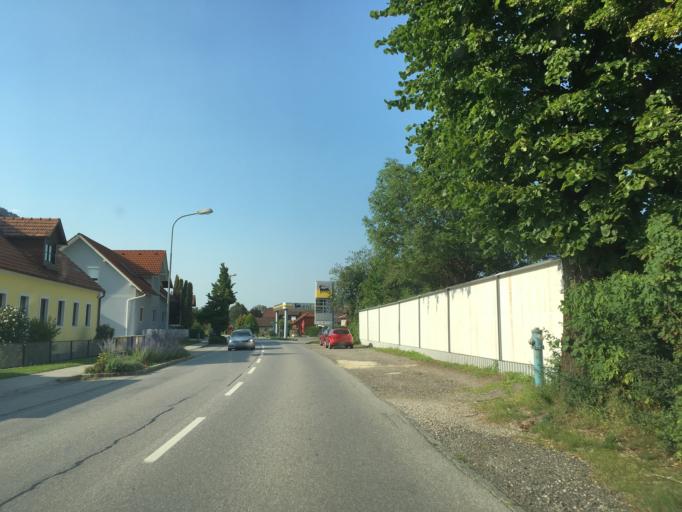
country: AT
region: Lower Austria
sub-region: Politischer Bezirk Neunkirchen
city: Grimmenstein
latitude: 47.6188
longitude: 16.1282
